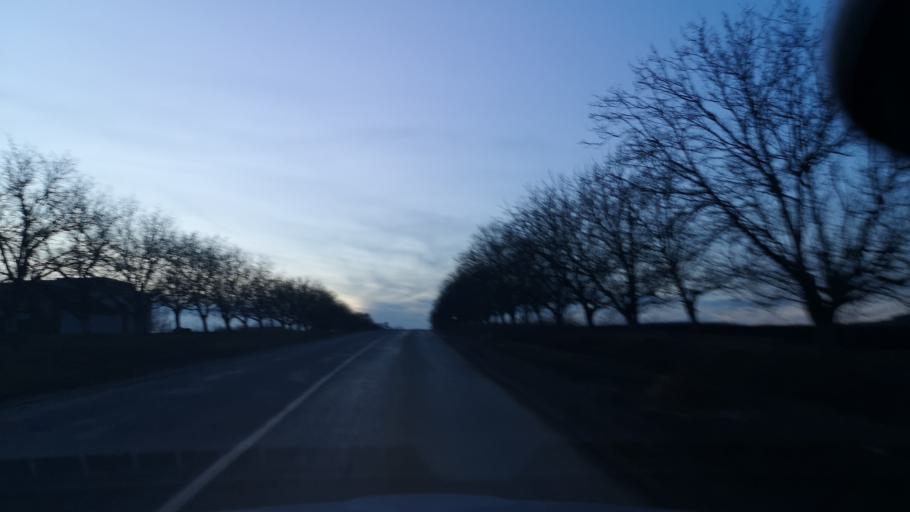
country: MD
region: Orhei
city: Orhei
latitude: 47.2835
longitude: 28.8408
